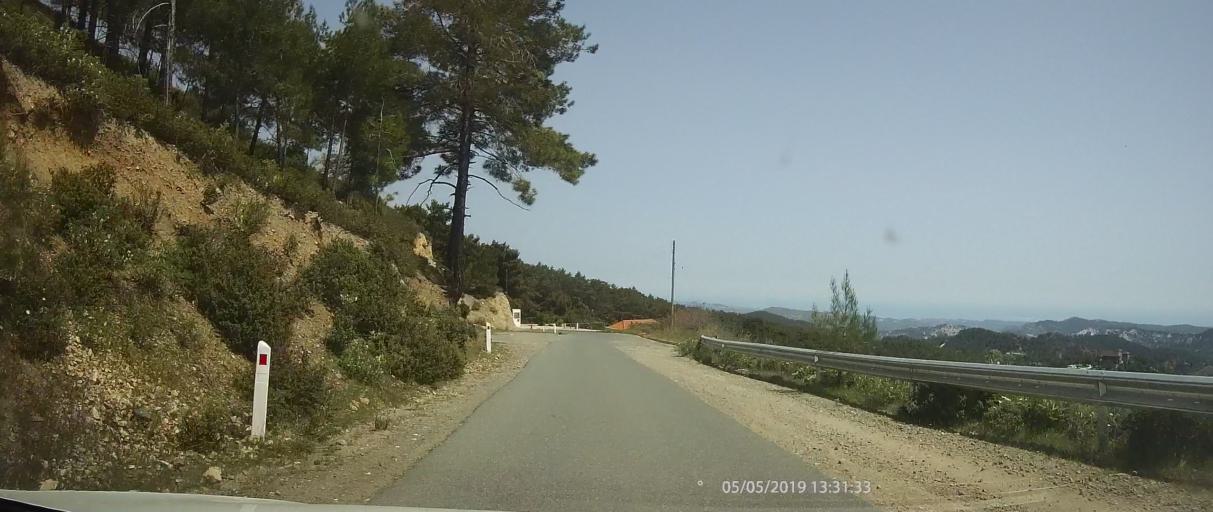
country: CY
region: Lefkosia
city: Kakopetria
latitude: 34.8917
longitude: 32.8496
